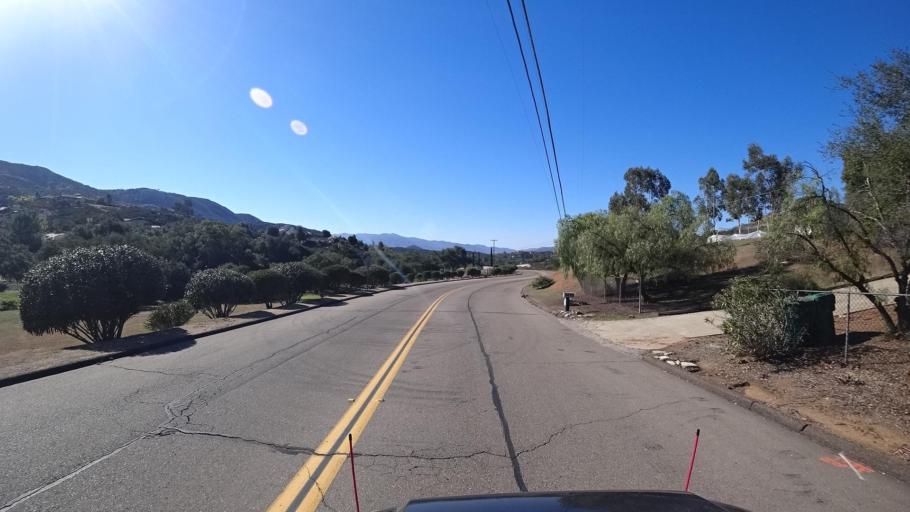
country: US
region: California
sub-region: San Diego County
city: Jamul
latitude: 32.7288
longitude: -116.8433
